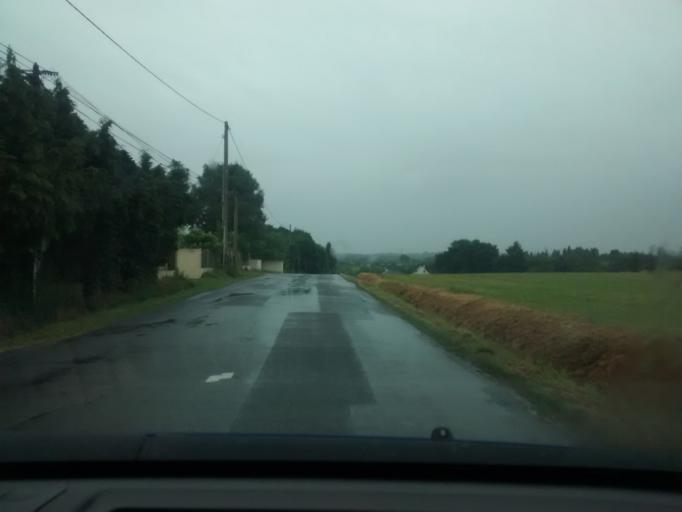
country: FR
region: Brittany
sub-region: Departement d'Ille-et-Vilaine
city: Betton
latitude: 48.1678
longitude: -1.6231
